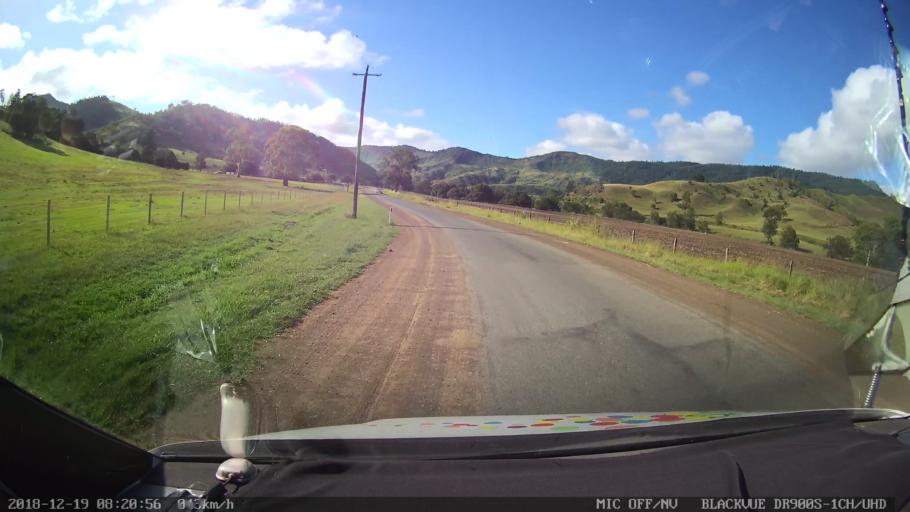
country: AU
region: New South Wales
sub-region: Kyogle
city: Kyogle
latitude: -28.2933
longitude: 152.9090
